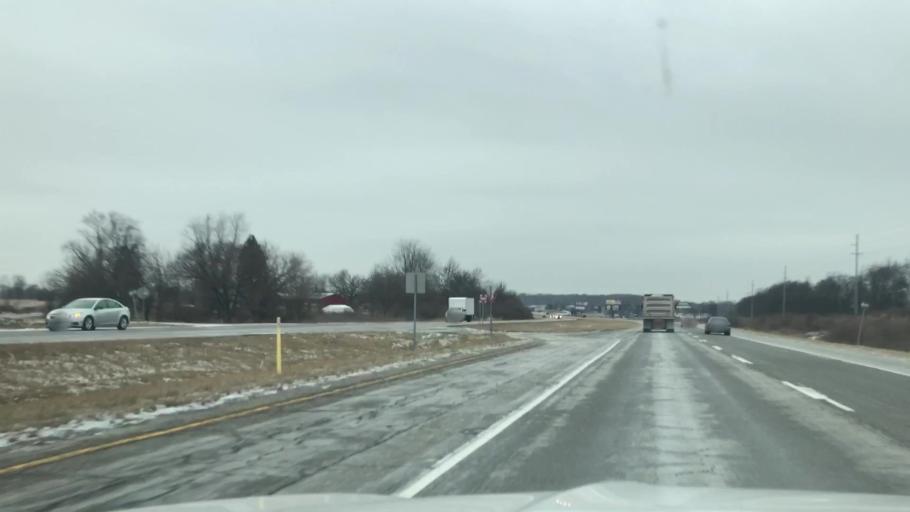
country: US
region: Indiana
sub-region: Fulton County
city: Rochester
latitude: 41.0274
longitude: -86.1809
